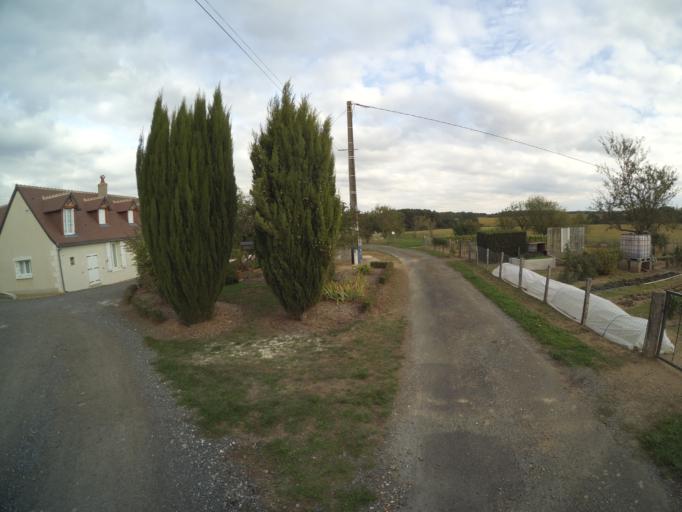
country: FR
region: Centre
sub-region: Departement d'Indre-et-Loire
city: Poce-sur-Cisse
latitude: 47.4786
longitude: 0.9629
